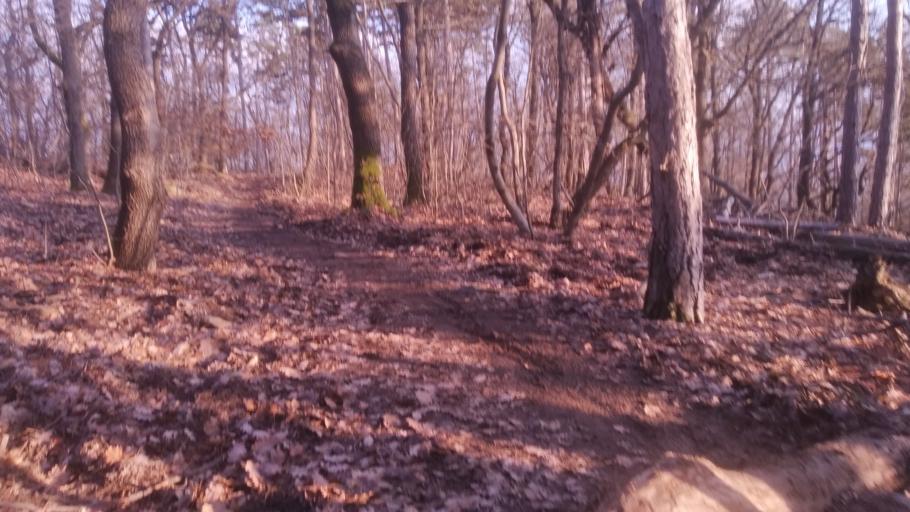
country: HU
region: Pest
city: Pilisborosjeno
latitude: 47.6123
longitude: 19.0032
